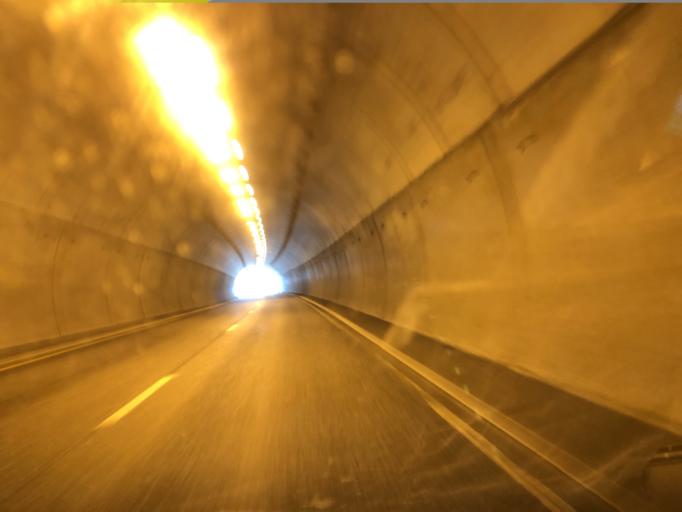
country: NO
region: Vestfold
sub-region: Larvik
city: Larvik
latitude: 59.0711
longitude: 9.9382
